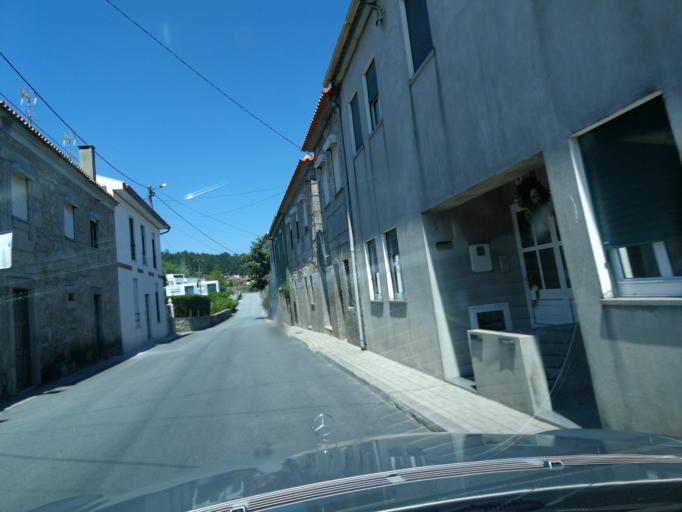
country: PT
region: Viana do Castelo
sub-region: Viana do Castelo
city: Meadela
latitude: 41.7324
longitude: -8.7864
